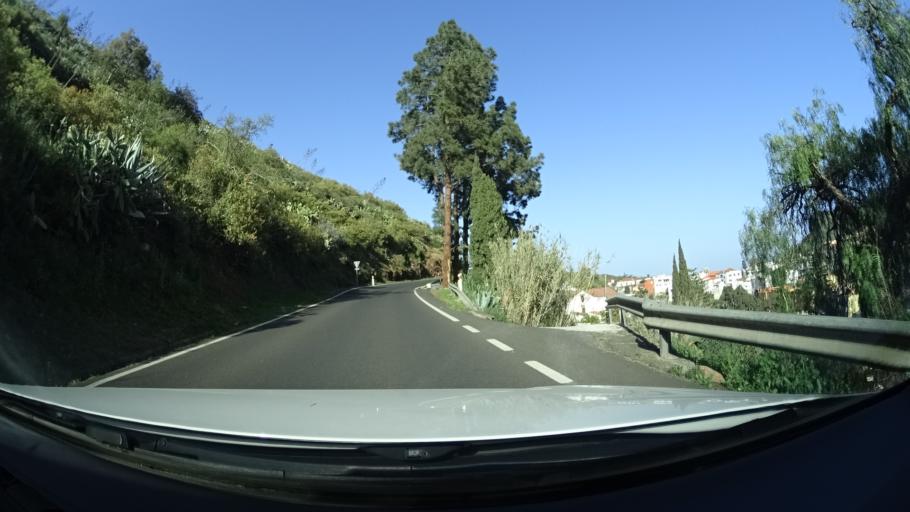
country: ES
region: Canary Islands
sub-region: Provincia de Las Palmas
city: Vega de San Mateo
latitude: 28.0101
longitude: -15.5360
